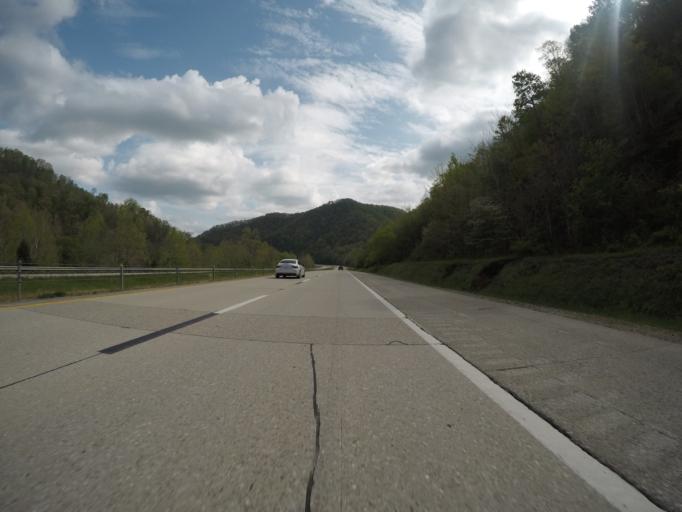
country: US
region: West Virginia
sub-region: Boone County
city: Madison
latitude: 38.1137
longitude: -81.8449
